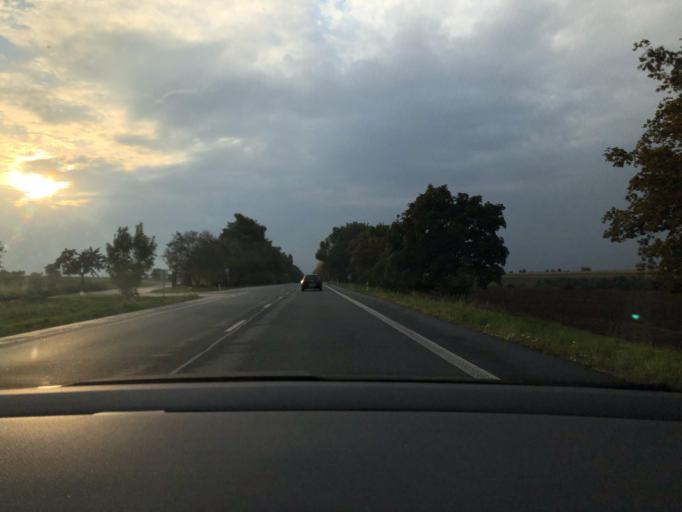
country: CZ
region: Central Bohemia
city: Velim
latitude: 50.0372
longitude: 15.1324
